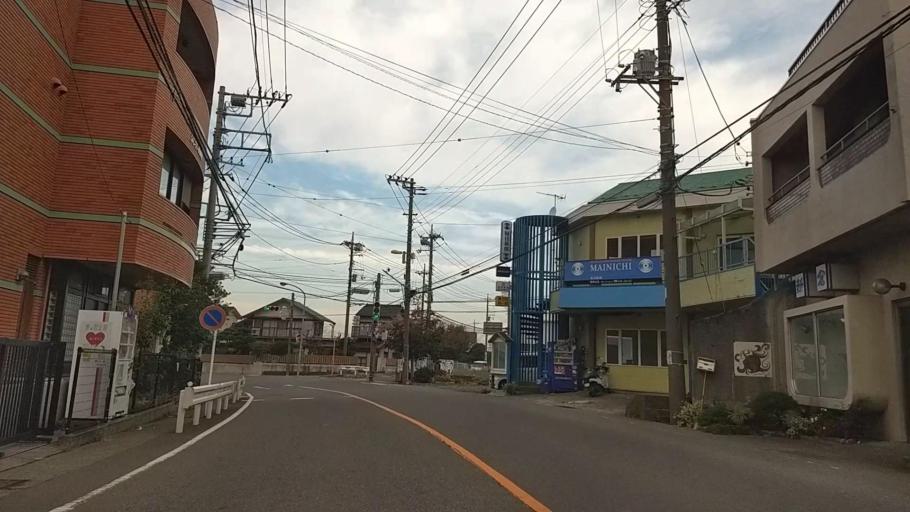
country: JP
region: Kanagawa
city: Fujisawa
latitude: 35.3974
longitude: 139.4404
